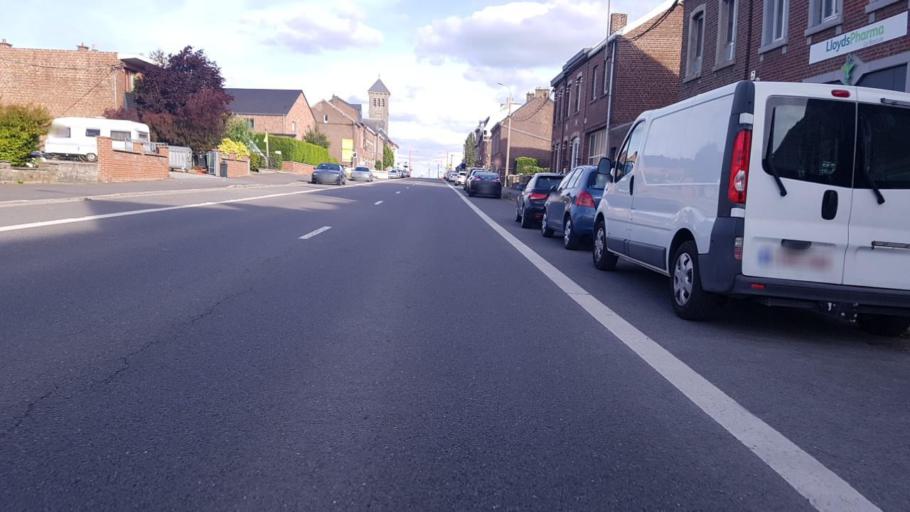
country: BE
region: Wallonia
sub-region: Province de Liege
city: Fleron
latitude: 50.6104
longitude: 5.7118
